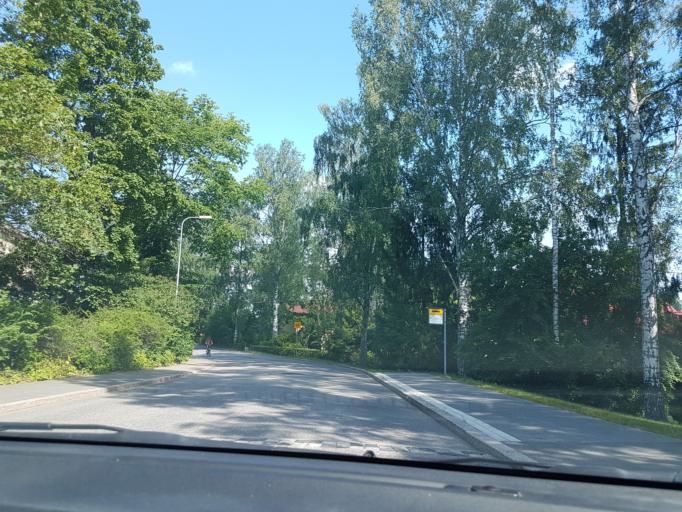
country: FI
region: Uusimaa
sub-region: Helsinki
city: Helsinki
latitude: 60.2595
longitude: 24.9536
